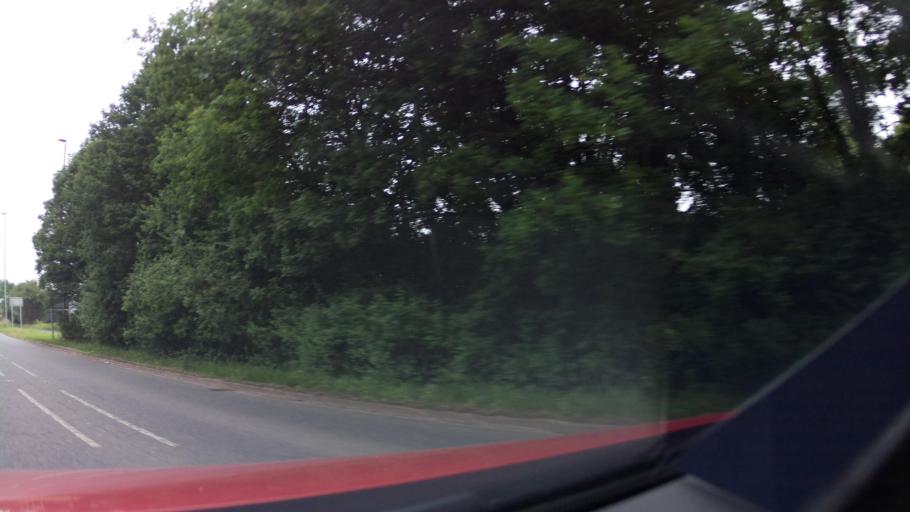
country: GB
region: England
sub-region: Leicestershire
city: Donisthorpe
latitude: 52.6915
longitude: -1.5509
